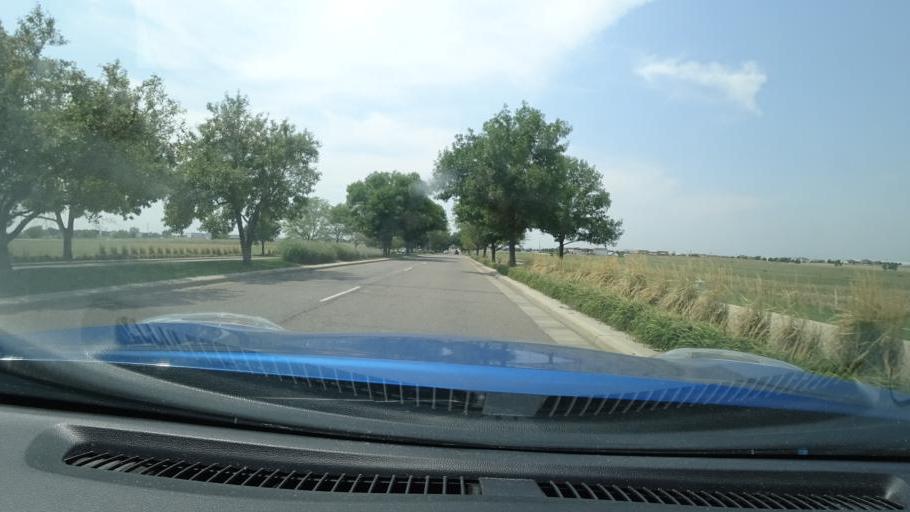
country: US
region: Colorado
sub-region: Adams County
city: Aurora
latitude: 39.7617
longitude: -104.7669
